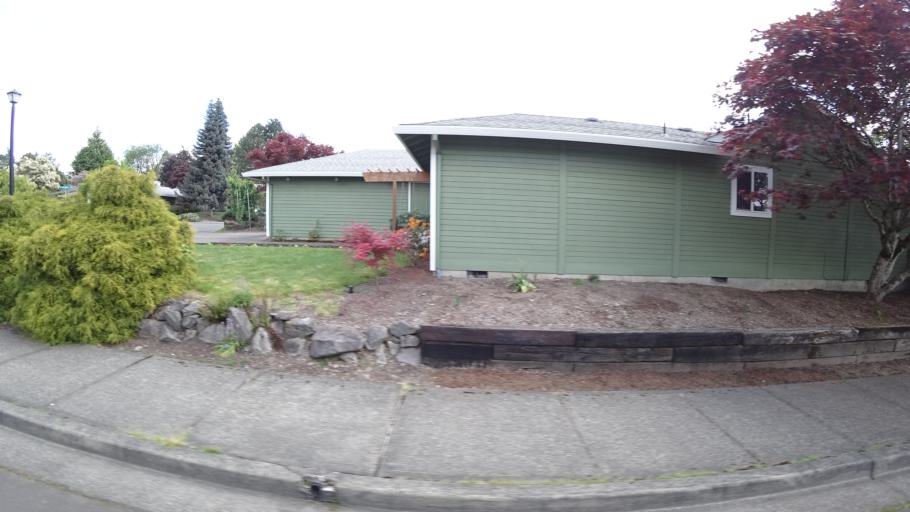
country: US
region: Oregon
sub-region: Washington County
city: Aloha
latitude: 45.5025
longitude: -122.8885
